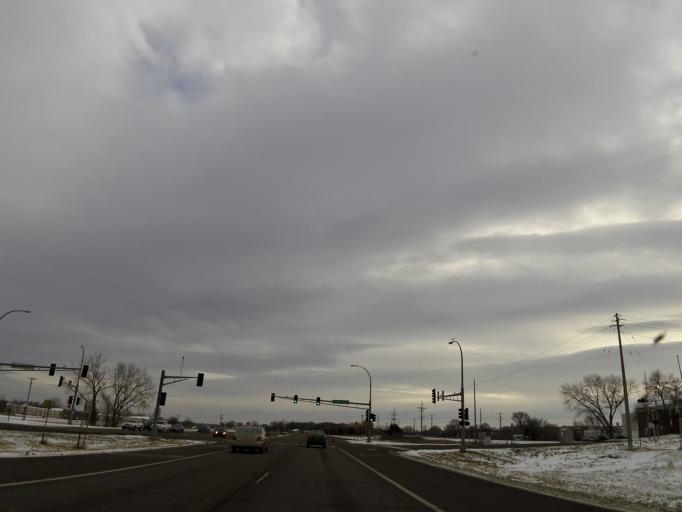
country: US
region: Minnesota
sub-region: Hennepin County
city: Eden Prairie
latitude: 44.7962
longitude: -93.4512
